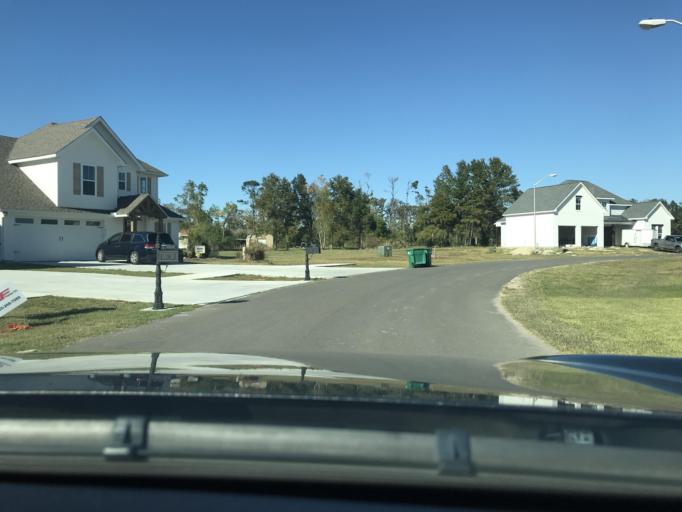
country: US
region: Louisiana
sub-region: Calcasieu Parish
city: Moss Bluff
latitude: 30.3132
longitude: -93.2576
